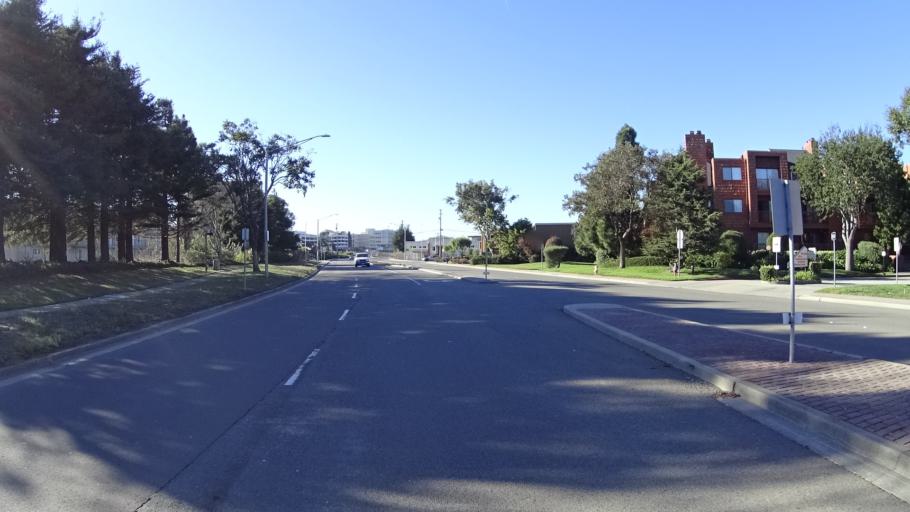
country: US
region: California
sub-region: San Mateo County
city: South San Francisco
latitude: 37.6571
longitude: -122.4331
